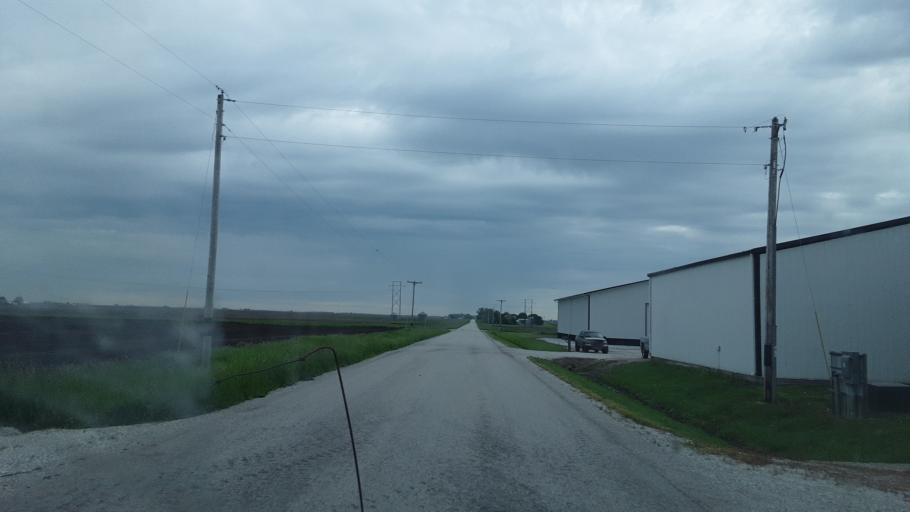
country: US
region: Illinois
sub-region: McDonough County
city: Macomb
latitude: 40.3812
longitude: -90.5279
